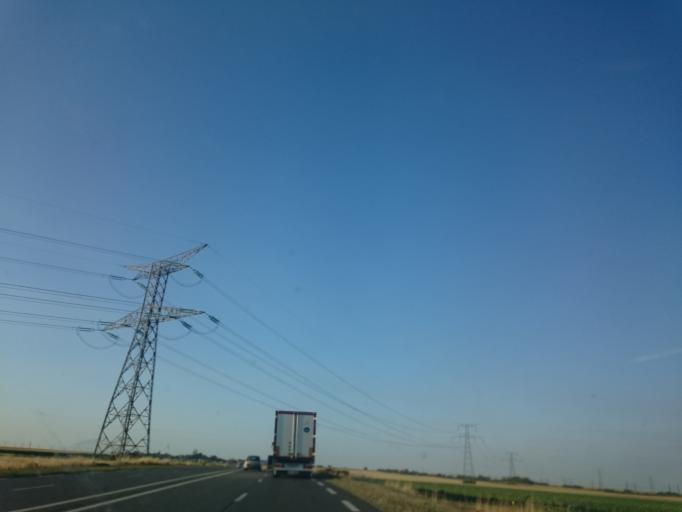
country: FR
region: Centre
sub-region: Departement du Loiret
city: Artenay
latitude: 48.1302
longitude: 1.9016
